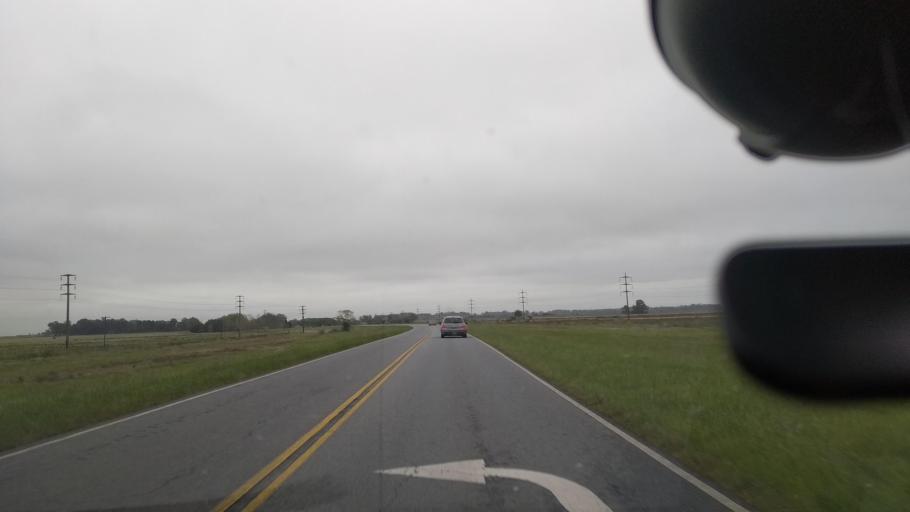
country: AR
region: Buenos Aires
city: Veronica
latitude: -35.3557
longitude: -57.4091
